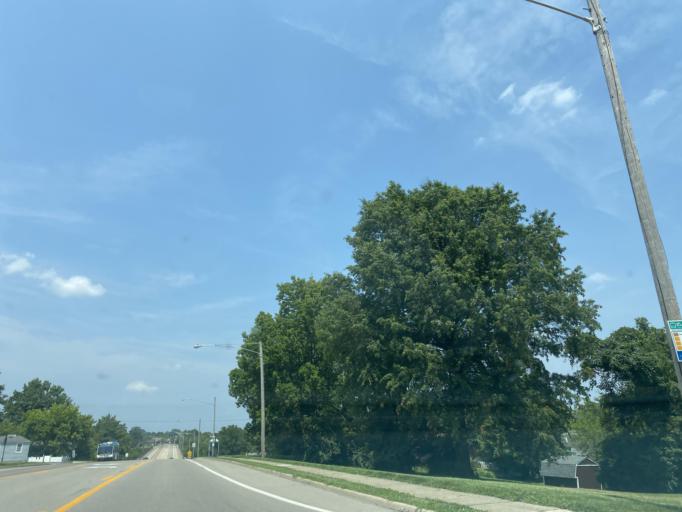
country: US
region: Kentucky
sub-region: Campbell County
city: Highland Heights
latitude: 39.0468
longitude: -84.4457
